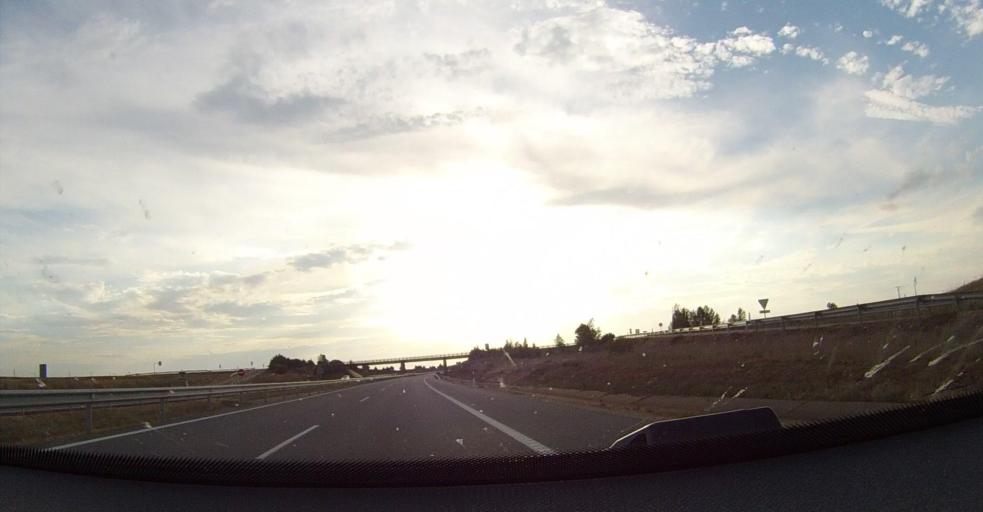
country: ES
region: Castille and Leon
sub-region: Provincia de Burgos
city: Melgar de Fernamental
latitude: 42.4018
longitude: -4.2119
